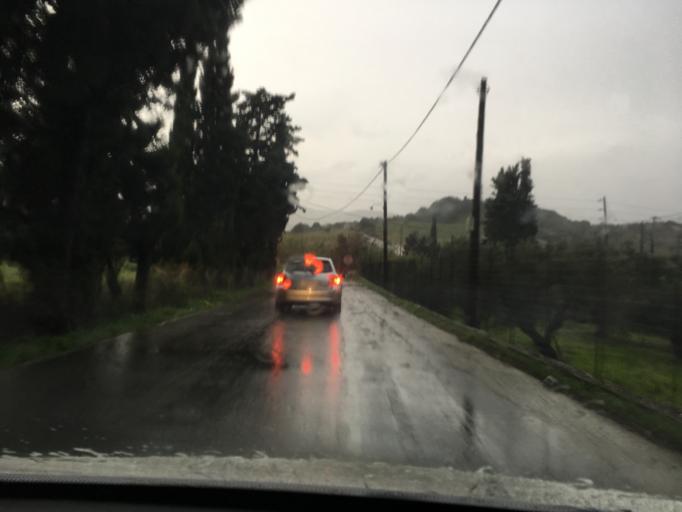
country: GR
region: West Greece
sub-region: Nomos Aitolias kai Akarnanias
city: Antirrio
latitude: 38.3417
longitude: 21.7673
